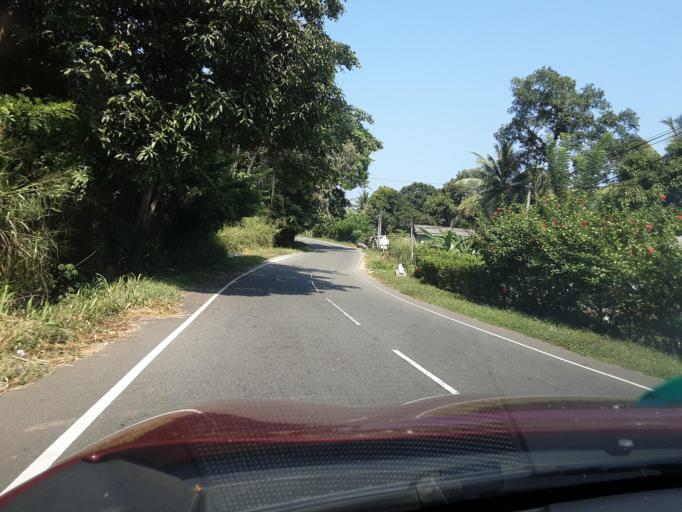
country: LK
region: Uva
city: Badulla
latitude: 7.1807
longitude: 81.0480
